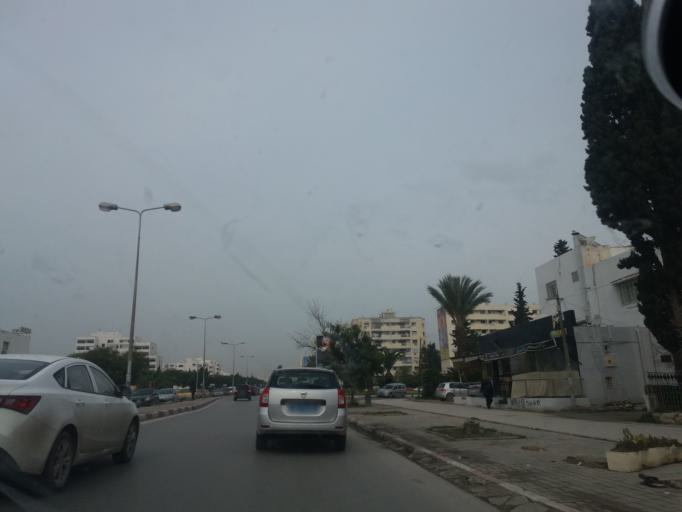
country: TN
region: Tunis
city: Tunis
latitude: 36.8427
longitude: 10.1664
